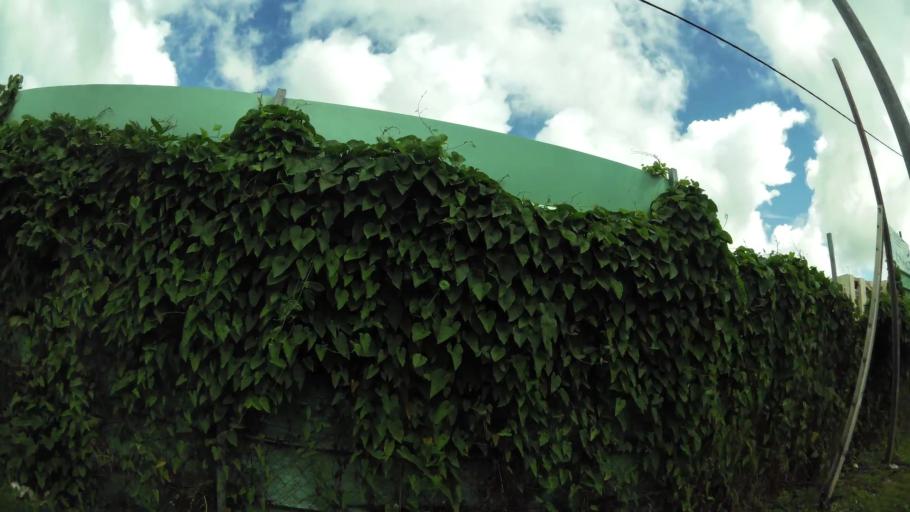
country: GP
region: Guadeloupe
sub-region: Guadeloupe
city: Pointe-a-Pitre
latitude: 16.2493
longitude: -61.5432
